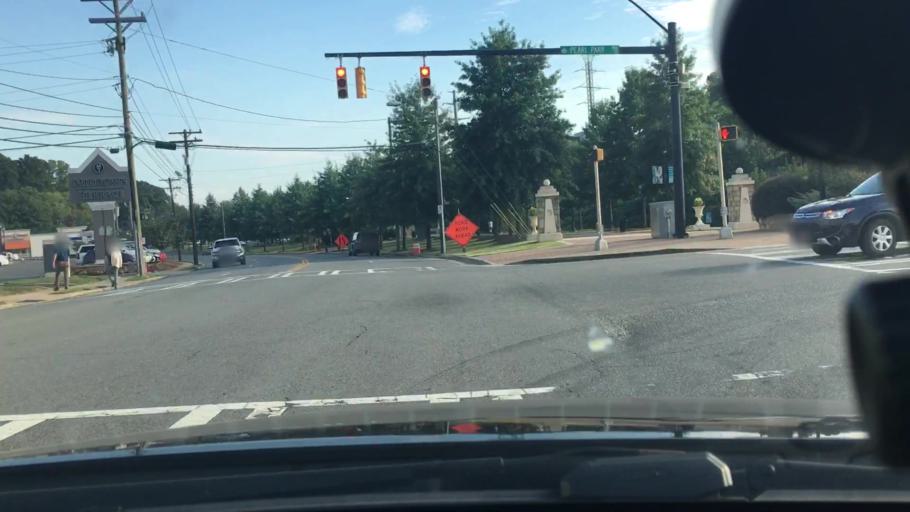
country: US
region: North Carolina
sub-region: Mecklenburg County
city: Charlotte
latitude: 35.2105
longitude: -80.8360
